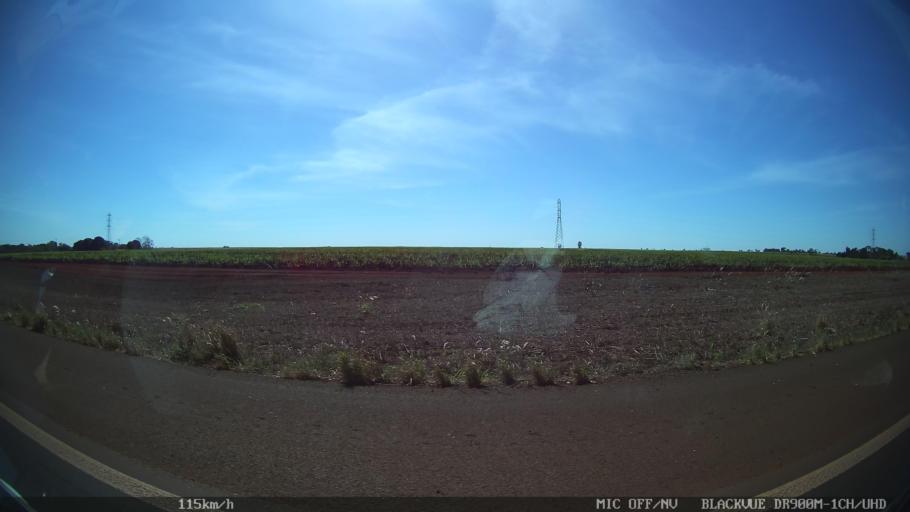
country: BR
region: Sao Paulo
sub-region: Guaira
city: Guaira
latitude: -20.4456
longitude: -48.4045
